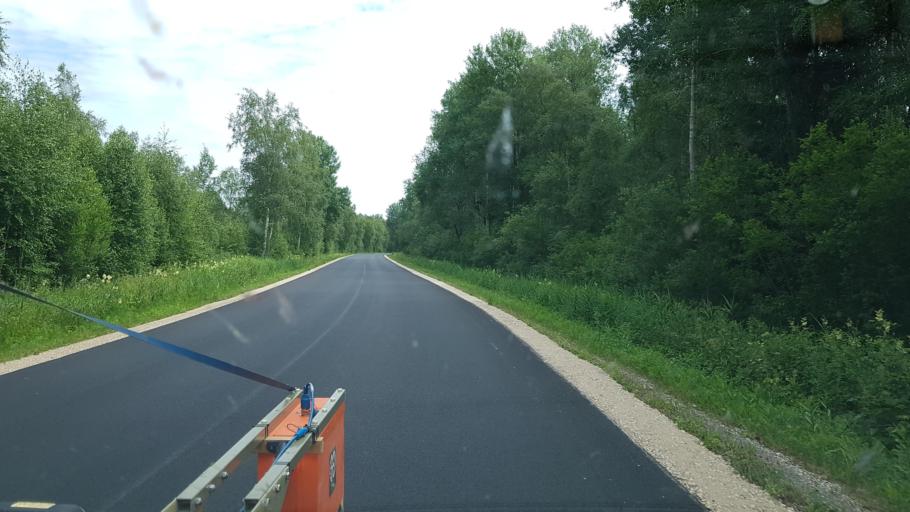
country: EE
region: Paernumaa
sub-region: Audru vald
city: Audru
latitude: 58.6232
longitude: 24.2535
